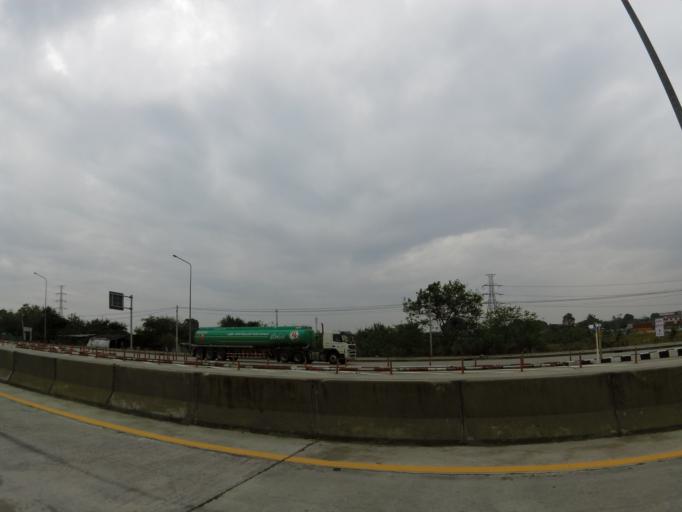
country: TH
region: Chon Buri
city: Ban Talat Bueng
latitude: 13.1161
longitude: 100.9754
